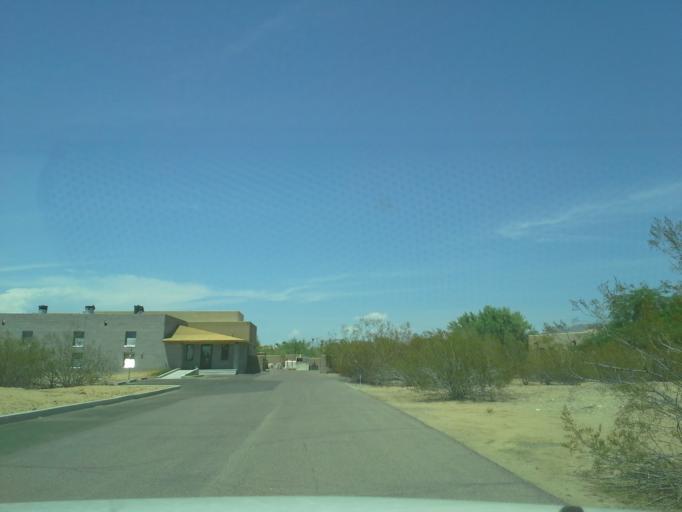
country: US
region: Arizona
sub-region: Maricopa County
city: Scottsdale
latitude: 33.5855
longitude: -111.8791
